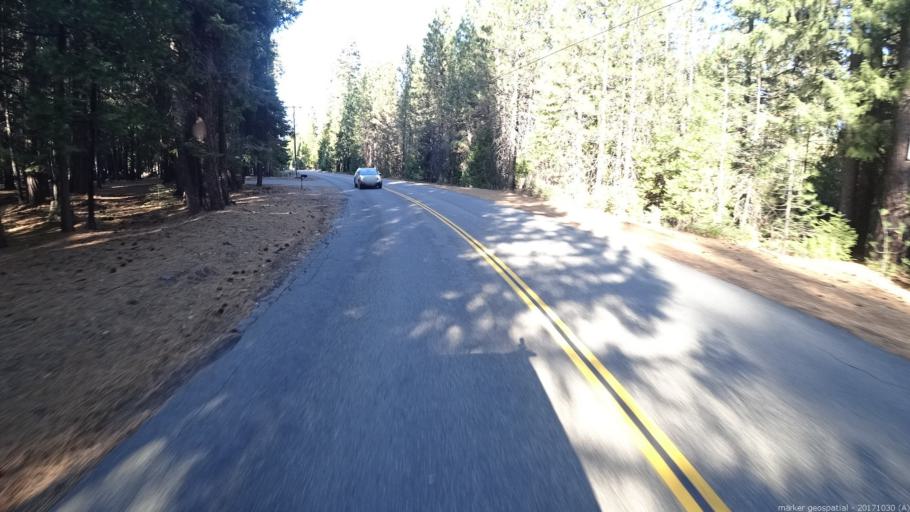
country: US
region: California
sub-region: Shasta County
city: Shingletown
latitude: 40.5253
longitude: -121.7472
